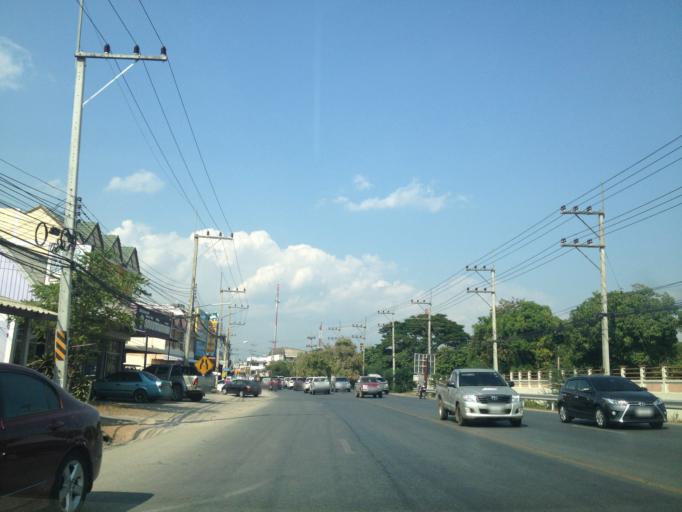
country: TH
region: Chiang Mai
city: San Pa Tong
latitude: 18.6160
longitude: 98.8975
